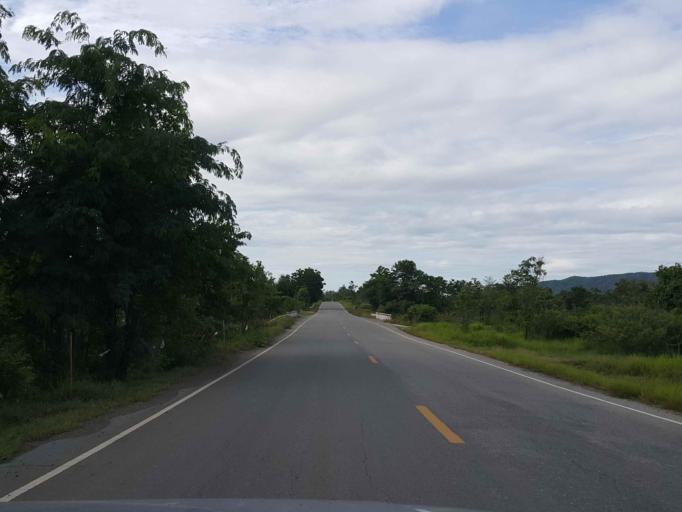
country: TH
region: Sukhothai
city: Thung Saliam
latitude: 17.2418
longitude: 99.5159
